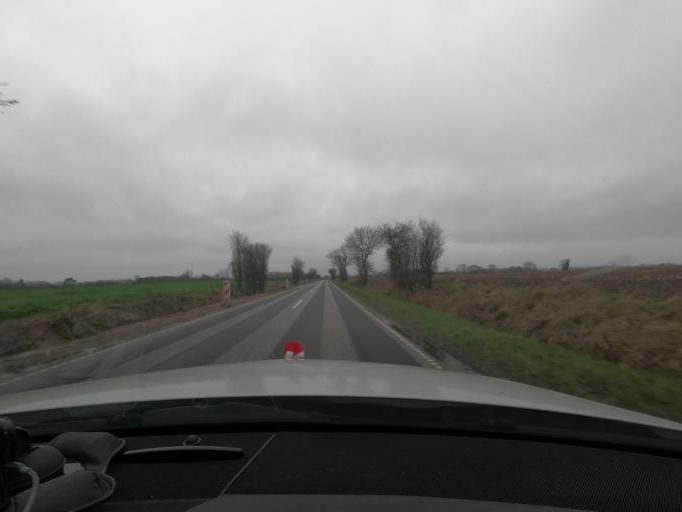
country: DK
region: South Denmark
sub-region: Haderslev Kommune
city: Starup
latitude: 55.2269
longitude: 9.6312
